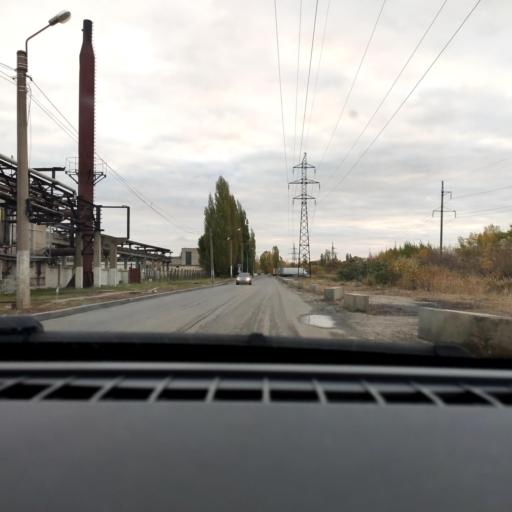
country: RU
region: Voronezj
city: Maslovka
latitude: 51.6235
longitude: 39.2475
